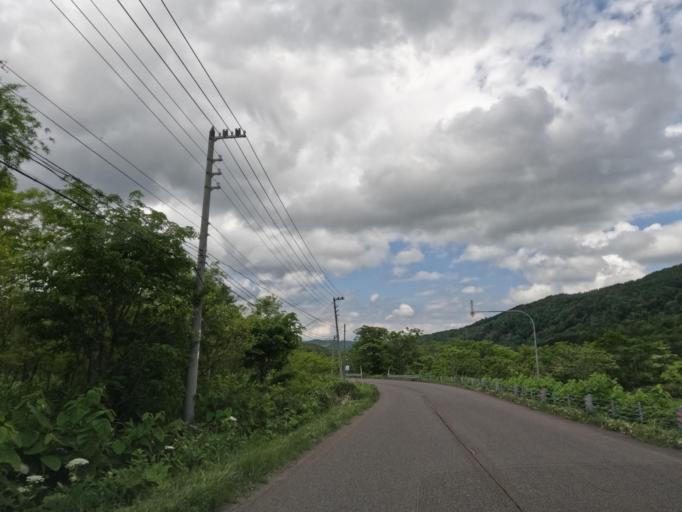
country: JP
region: Hokkaido
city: Takikawa
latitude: 43.5726
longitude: 141.7099
